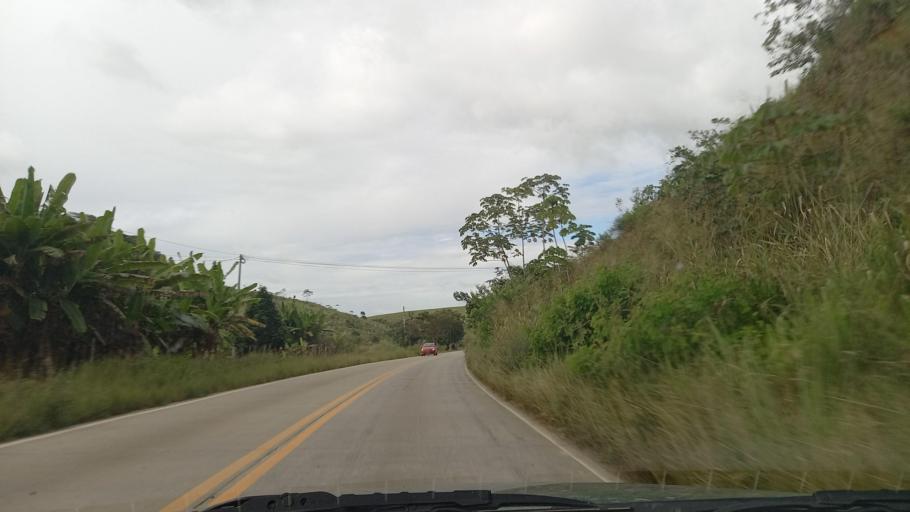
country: BR
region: Pernambuco
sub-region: Maraial
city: Maraial
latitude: -8.7607
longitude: -35.8556
